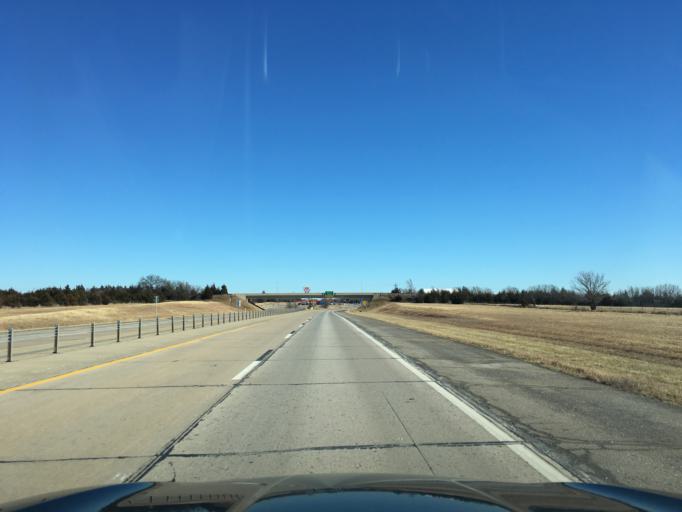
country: US
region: Oklahoma
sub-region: Pawnee County
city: Pawnee
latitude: 36.2248
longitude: -96.8056
